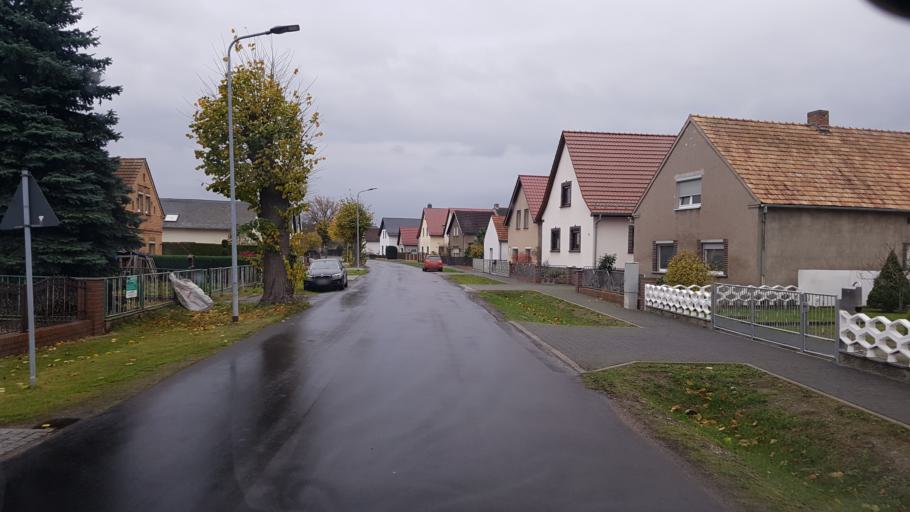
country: DE
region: Brandenburg
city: Ortrand
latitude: 51.4111
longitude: 13.7714
